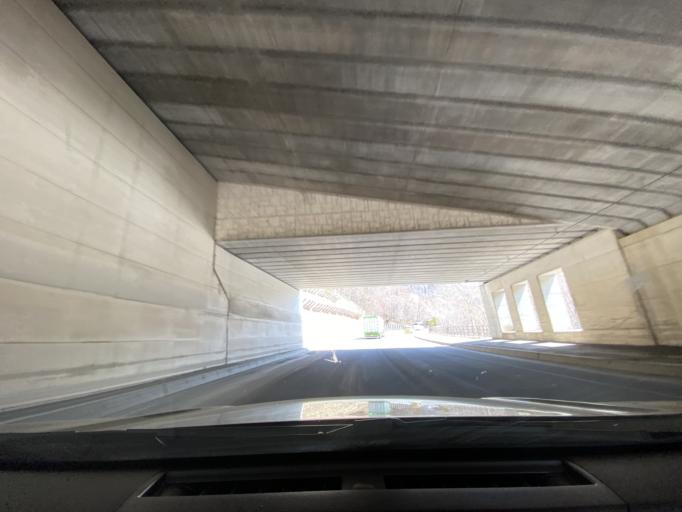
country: JP
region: Hokkaido
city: Kamikawa
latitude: 43.7265
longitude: 142.9645
